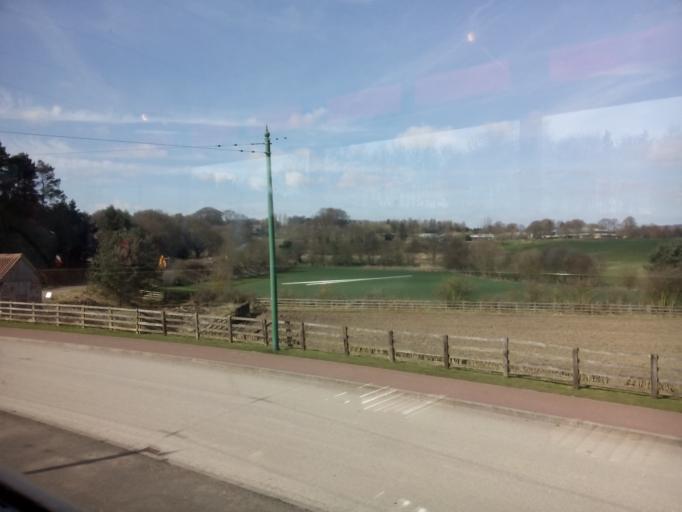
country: GB
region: England
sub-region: County Durham
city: Stanley
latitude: 54.8848
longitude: -1.6573
